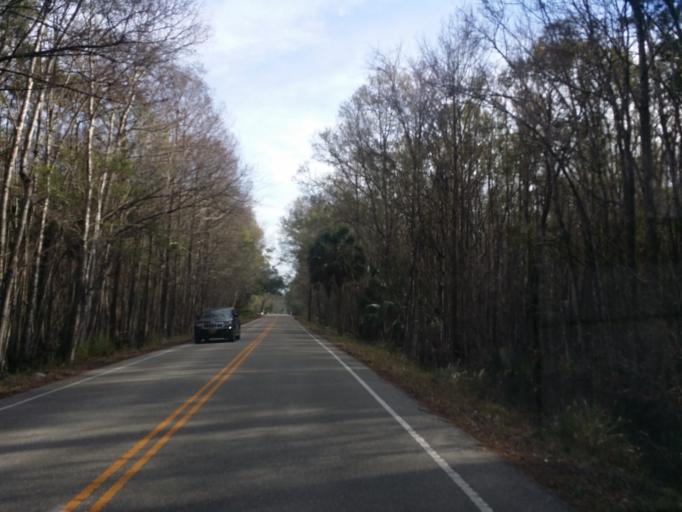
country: US
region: Florida
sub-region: Leon County
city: Woodville
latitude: 30.1468
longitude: -84.1419
